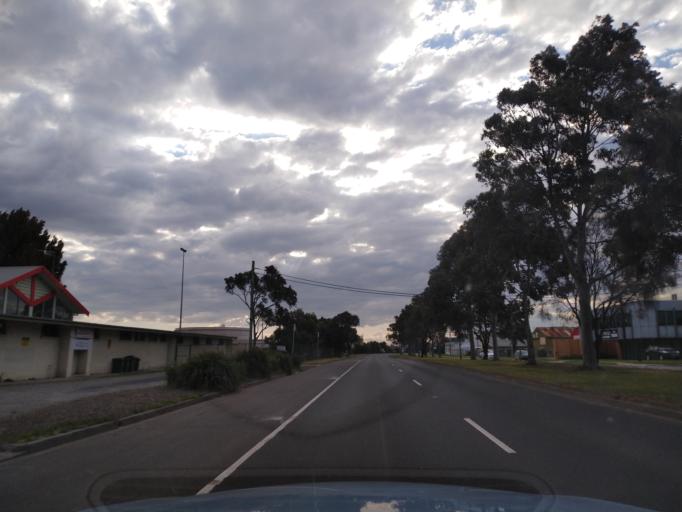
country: AU
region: Victoria
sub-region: Hobsons Bay
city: Williamstown North
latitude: -37.8555
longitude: 144.8656
